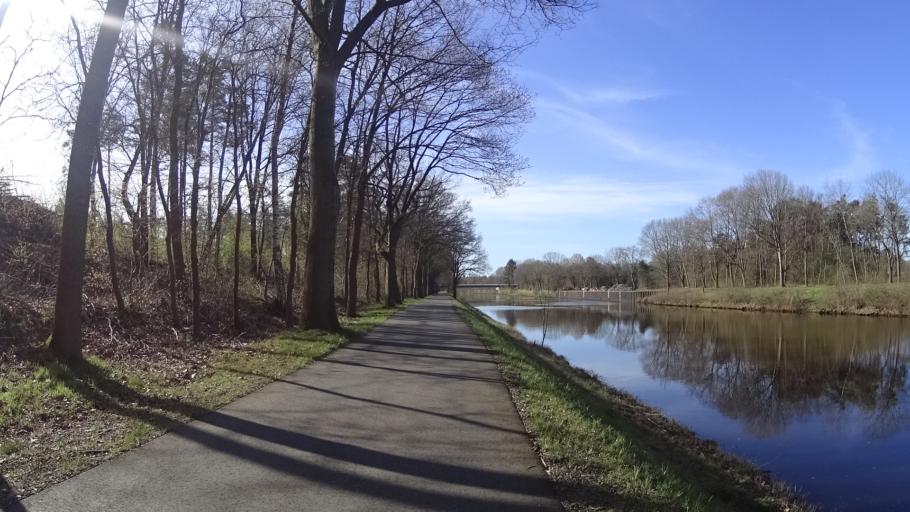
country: DE
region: Lower Saxony
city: Meppen
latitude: 52.7374
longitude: 7.2607
